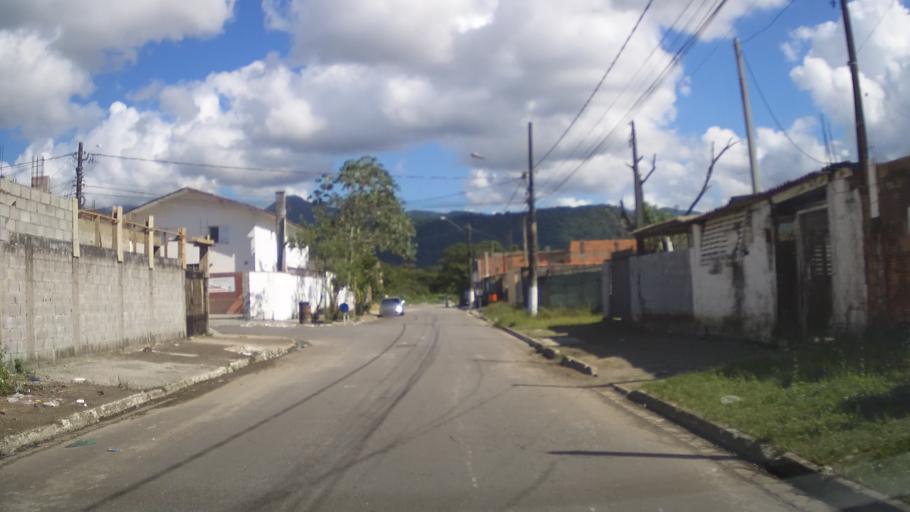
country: BR
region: Sao Paulo
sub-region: Praia Grande
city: Praia Grande
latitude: -24.0171
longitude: -46.5134
